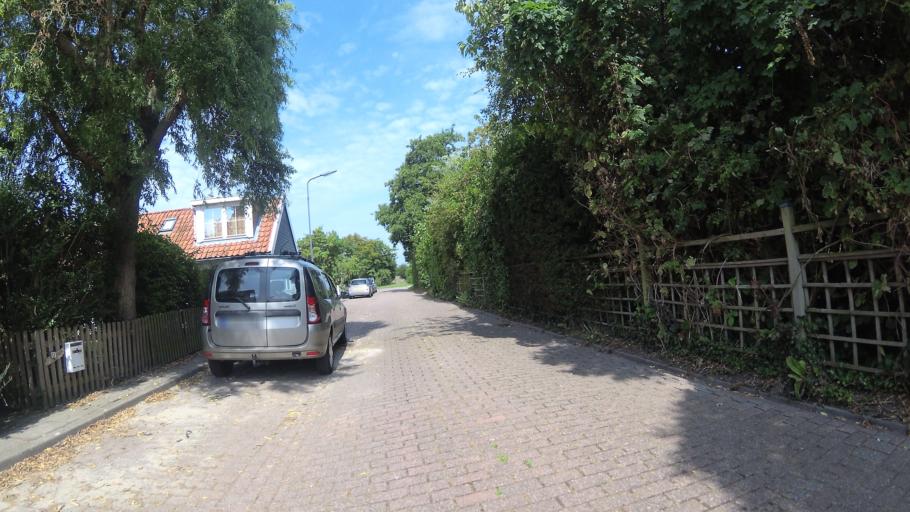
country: NL
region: Zeeland
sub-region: Gemeente Noord-Beveland
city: Kamperland
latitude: 51.5875
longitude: 3.7479
